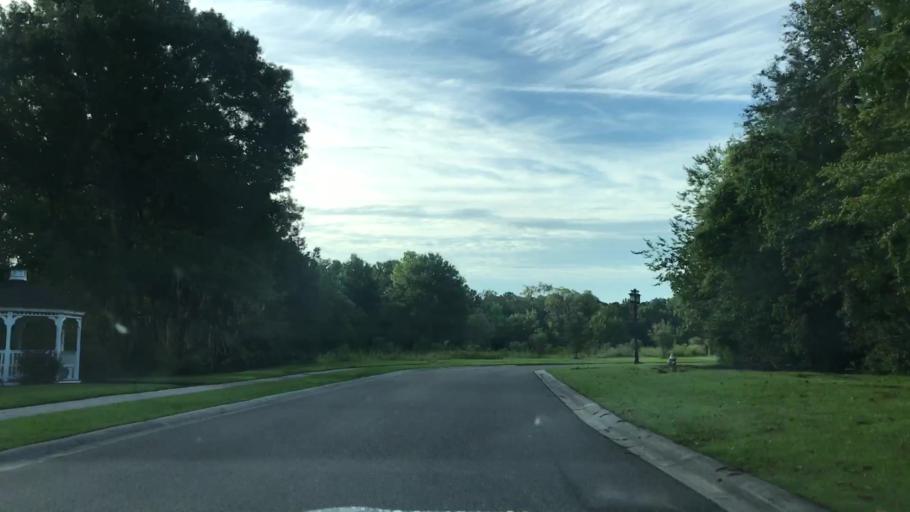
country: US
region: South Carolina
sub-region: Charleston County
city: Shell Point
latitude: 32.8352
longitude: -80.0699
